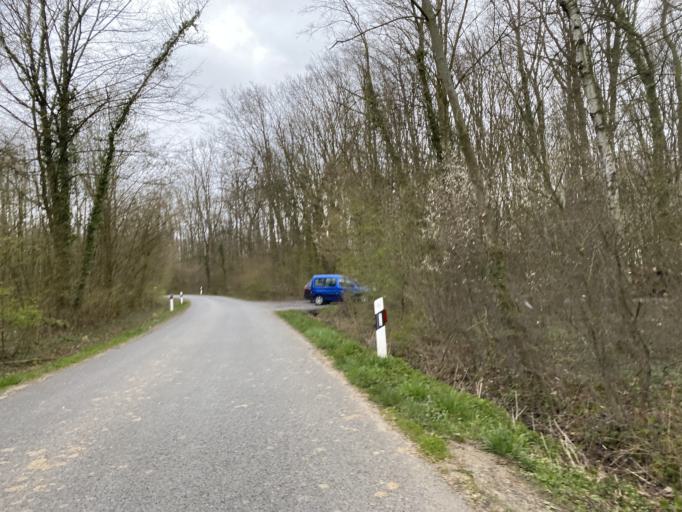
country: DE
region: North Rhine-Westphalia
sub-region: Regierungsbezirk Arnsberg
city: Welver
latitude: 51.6823
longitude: 7.9145
